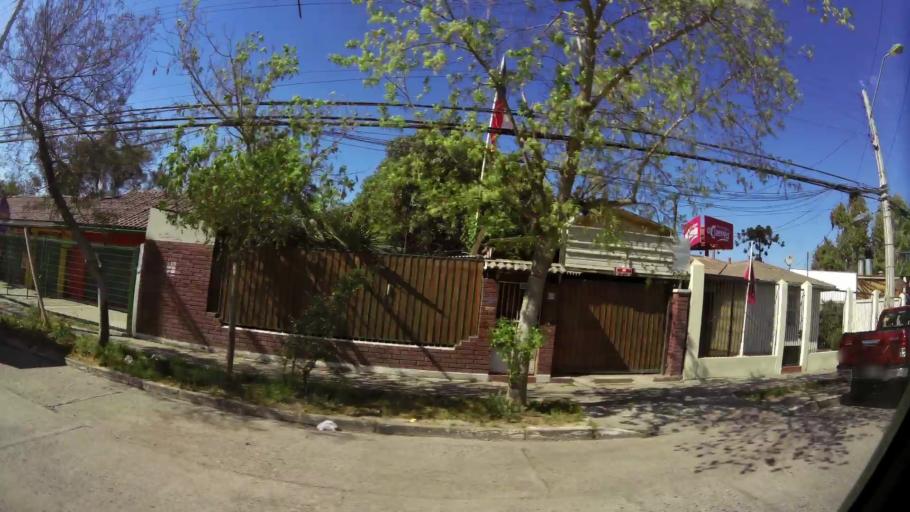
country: CL
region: Santiago Metropolitan
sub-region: Provincia de Talagante
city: Penaflor
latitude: -33.6068
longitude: -70.8985
